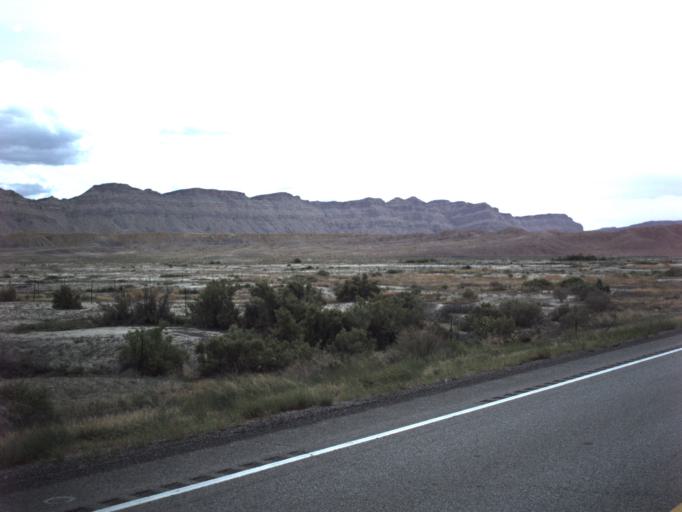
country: US
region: Utah
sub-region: Carbon County
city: East Carbon City
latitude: 39.3255
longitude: -110.3666
